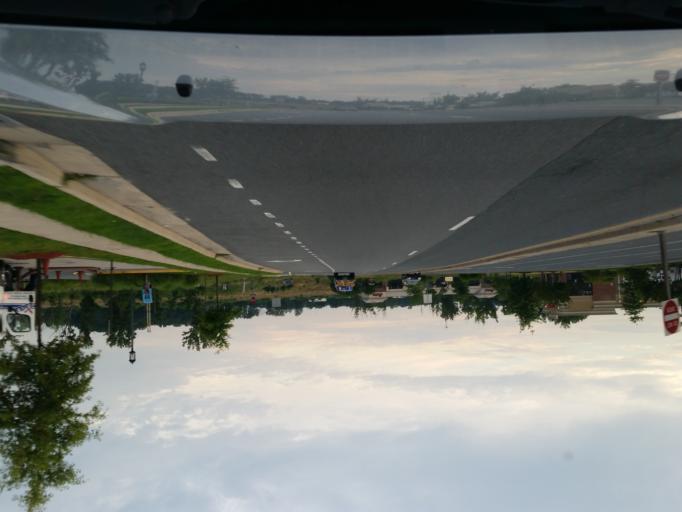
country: US
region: Virginia
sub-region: City of Fredericksburg
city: Fredericksburg
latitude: 38.2385
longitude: -77.5063
